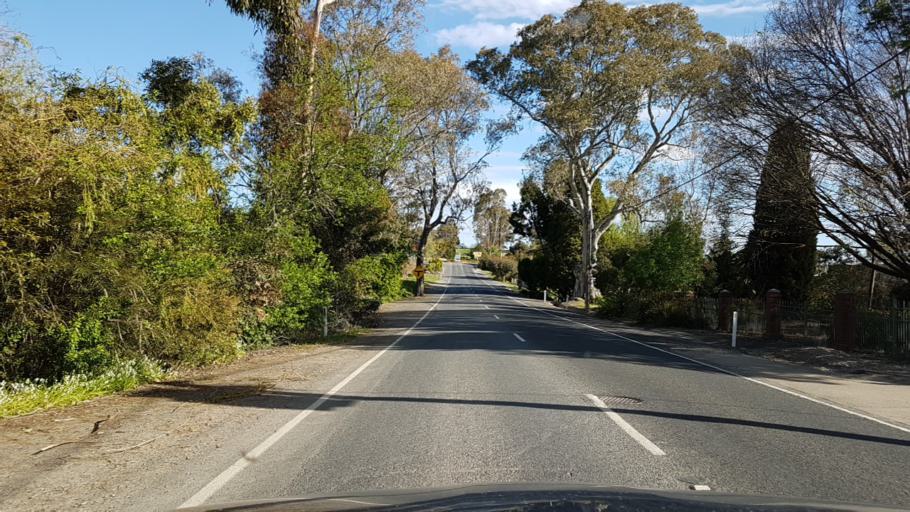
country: AU
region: South Australia
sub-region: Adelaide Hills
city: Lobethal
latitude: -34.8940
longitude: 138.8794
